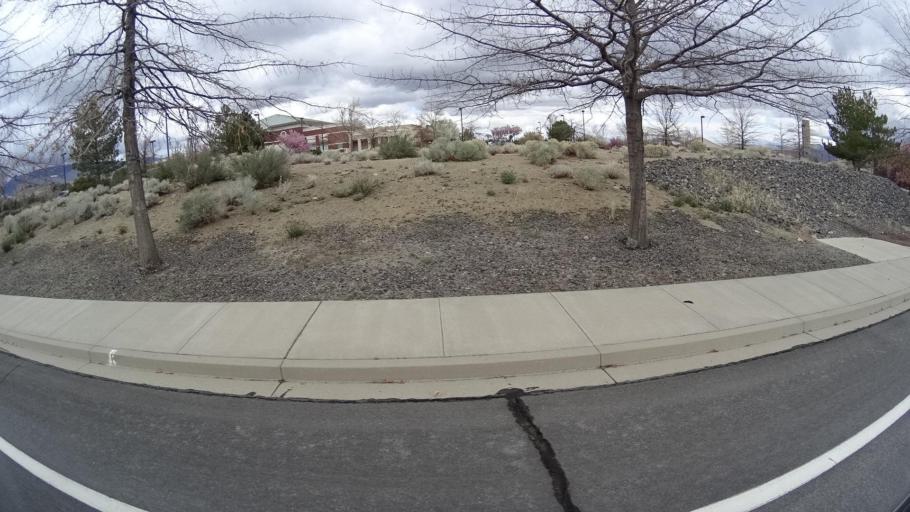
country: US
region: Nevada
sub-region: Storey County
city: Virginia City
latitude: 39.3898
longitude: -119.7688
